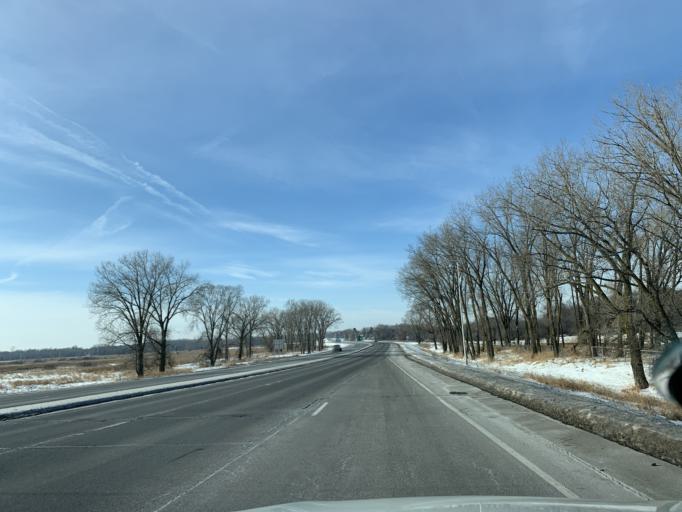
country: US
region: Minnesota
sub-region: Washington County
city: Forest Lake
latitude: 45.2893
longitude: -92.9899
